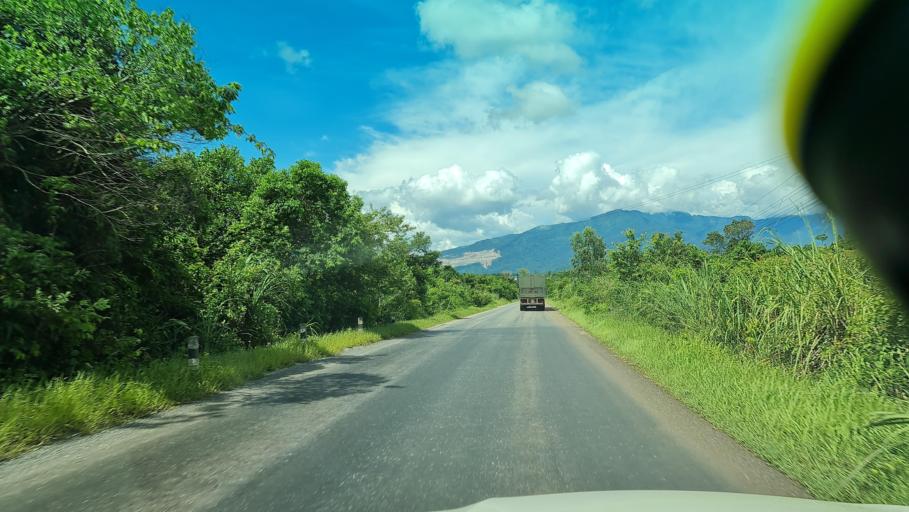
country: LA
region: Bolikhamxai
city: Pakkading
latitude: 18.2889
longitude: 104.0763
